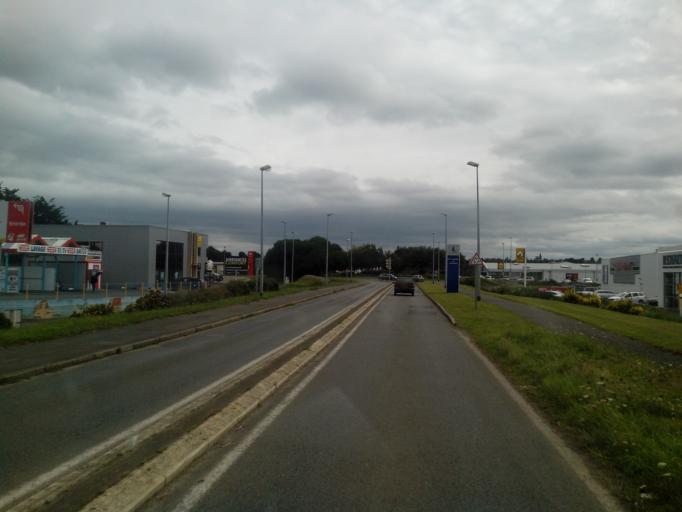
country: FR
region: Brittany
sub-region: Departement des Cotes-d'Armor
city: Saint-Quay-Portrieux
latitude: 48.6443
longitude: -2.8375
